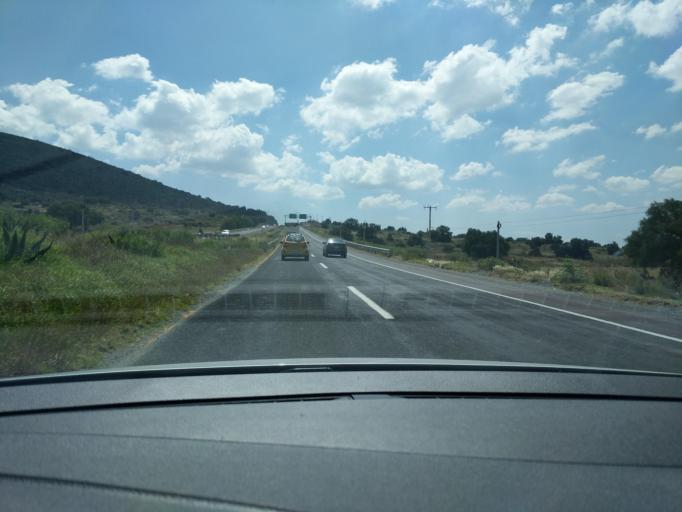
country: MX
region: Hidalgo
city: Zempoala
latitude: 19.8975
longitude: -98.6713
